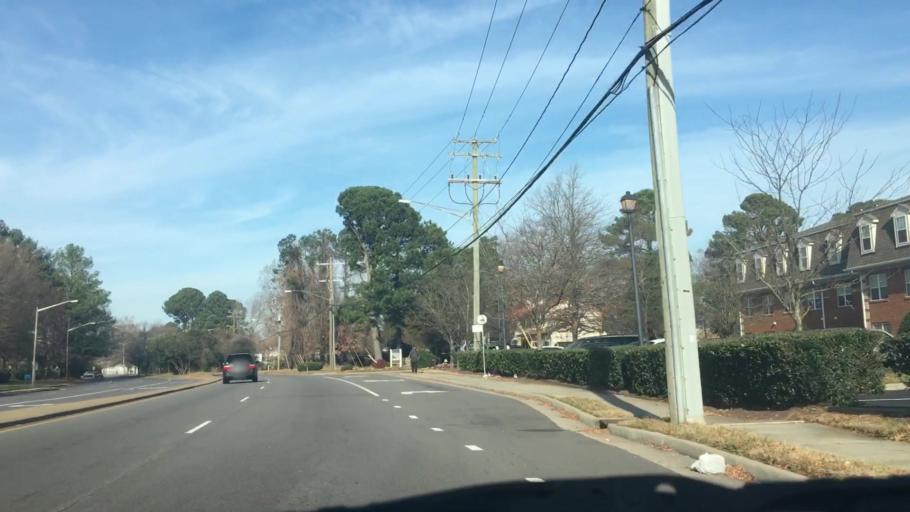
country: US
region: Virginia
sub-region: City of Chesapeake
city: Chesapeake
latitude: 36.8232
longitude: -76.1521
